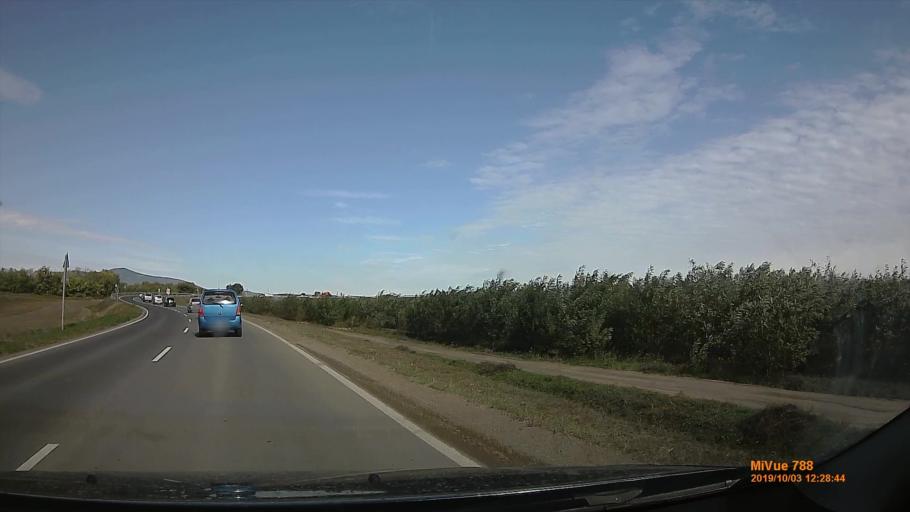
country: HU
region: Pest
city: Szodliget
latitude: 47.7313
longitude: 19.1588
